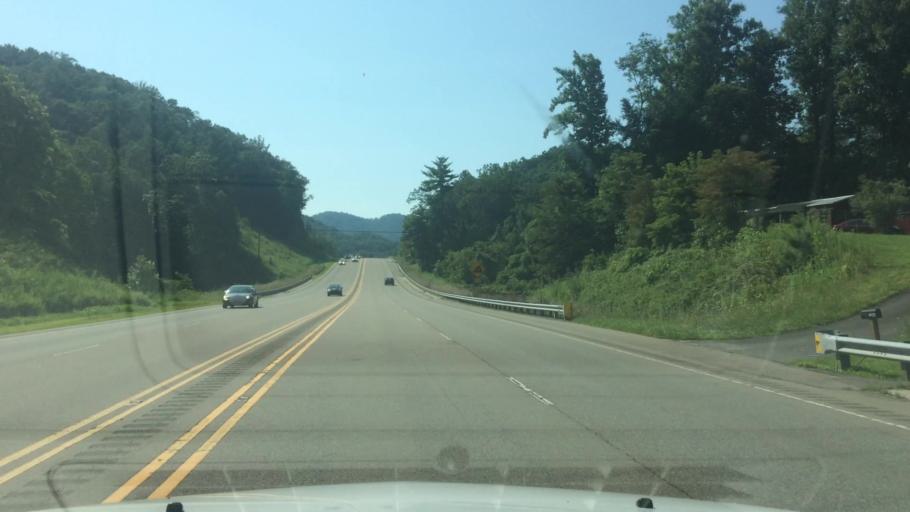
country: US
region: North Carolina
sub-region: Watauga County
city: Blowing Rock
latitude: 36.0603
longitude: -81.6035
